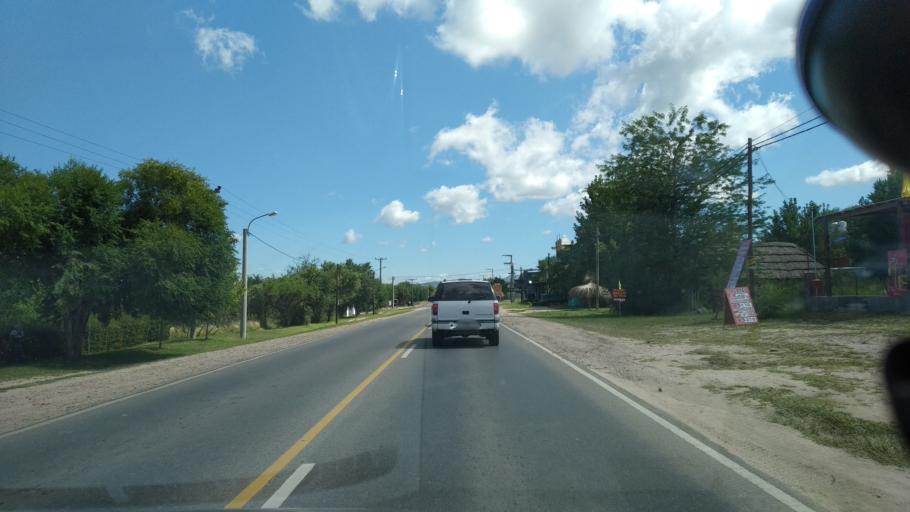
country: AR
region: Cordoba
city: Mina Clavero
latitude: -31.7722
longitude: -65.0006
